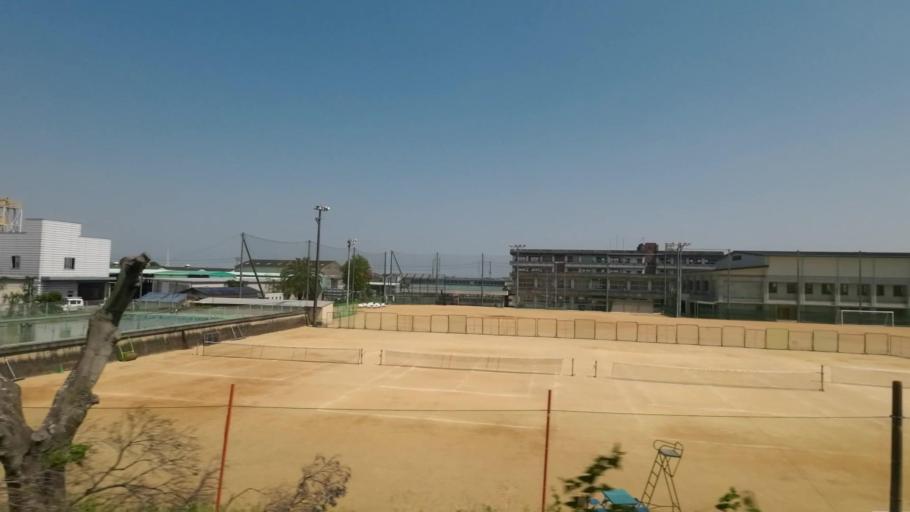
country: JP
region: Ehime
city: Saijo
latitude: 33.8965
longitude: 133.1363
